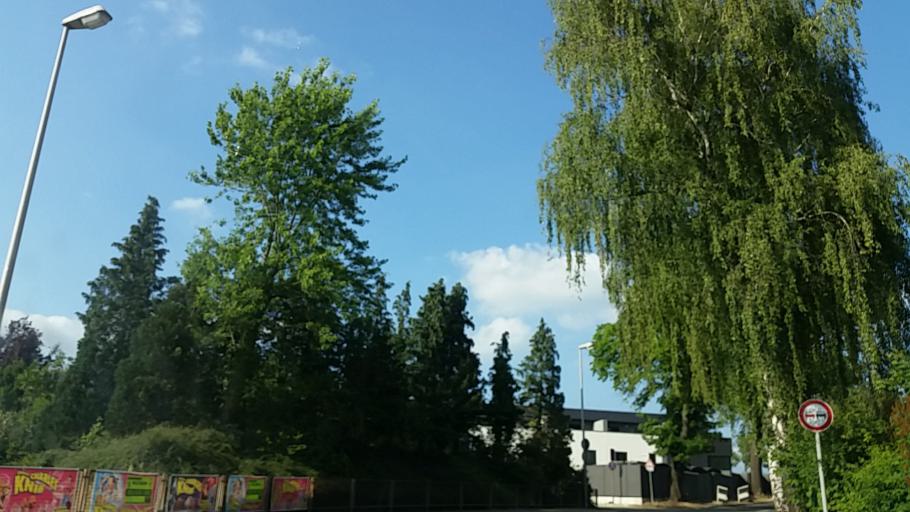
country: DE
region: Lower Saxony
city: Weyhausen
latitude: 52.4017
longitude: 10.6973
